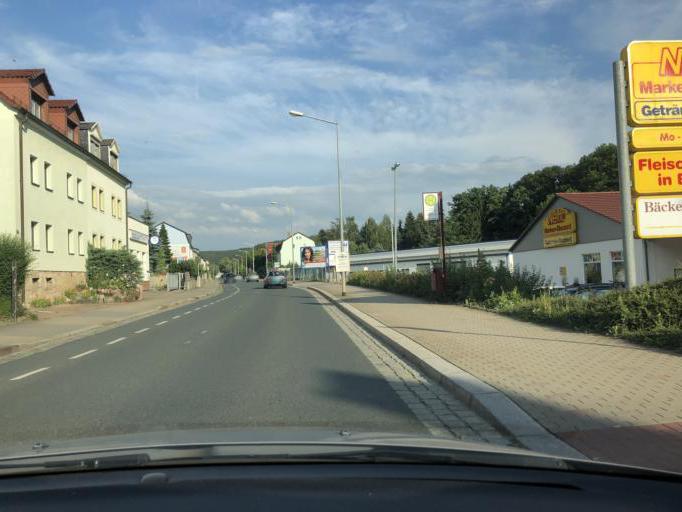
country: DE
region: Saxony
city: Freital
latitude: 50.9915
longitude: 13.6598
